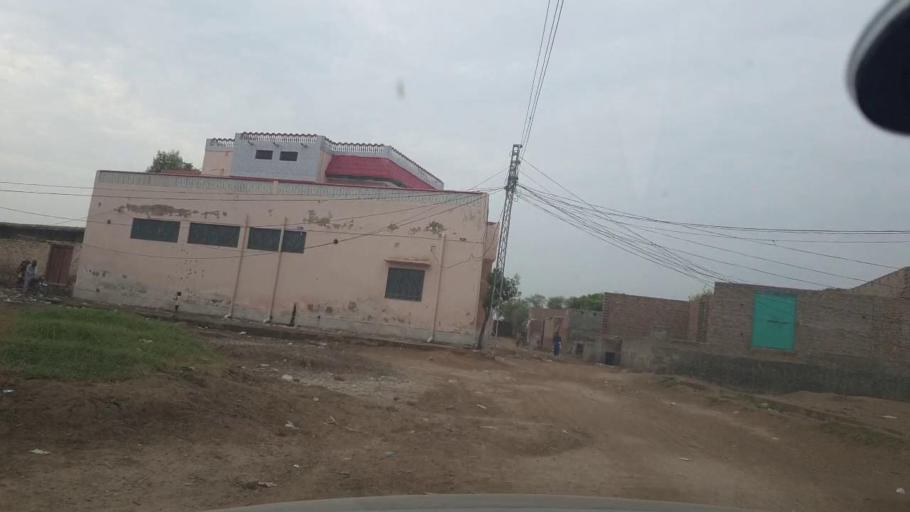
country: PK
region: Sindh
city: Jacobabad
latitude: 28.2567
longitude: 68.4510
